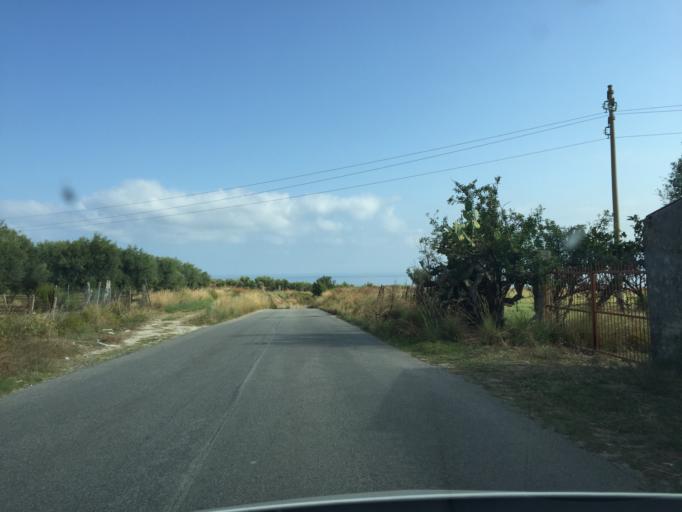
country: IT
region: Calabria
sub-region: Provincia di Vibo-Valentia
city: Pannaconi
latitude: 38.7136
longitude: 16.0490
